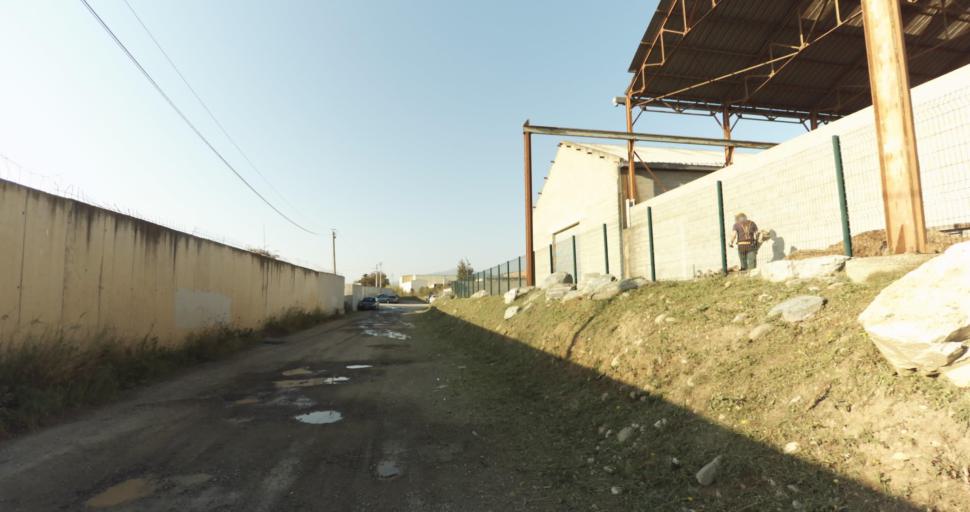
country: FR
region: Corsica
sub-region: Departement de la Haute-Corse
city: Biguglia
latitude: 42.6003
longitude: 9.4461
